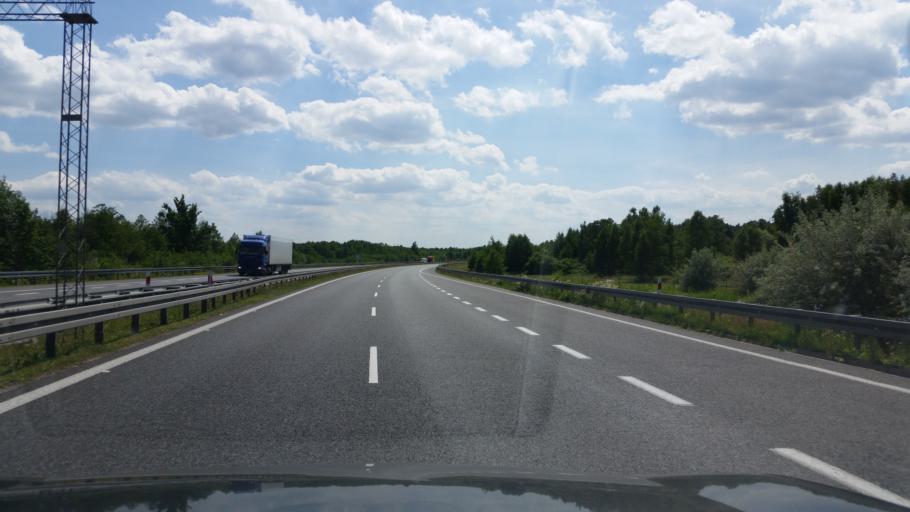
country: PL
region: Masovian Voivodeship
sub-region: Powiat wyszkowski
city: Wyszkow
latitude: 52.5855
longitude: 21.4983
